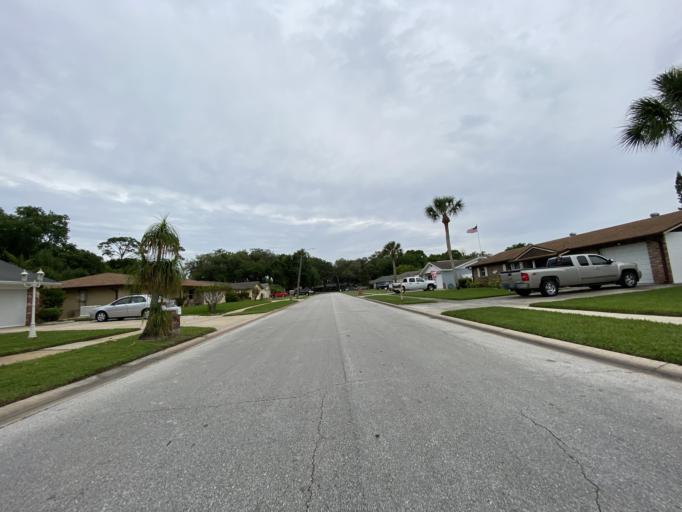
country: US
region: Florida
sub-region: Volusia County
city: South Daytona
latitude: 29.1528
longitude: -81.0035
